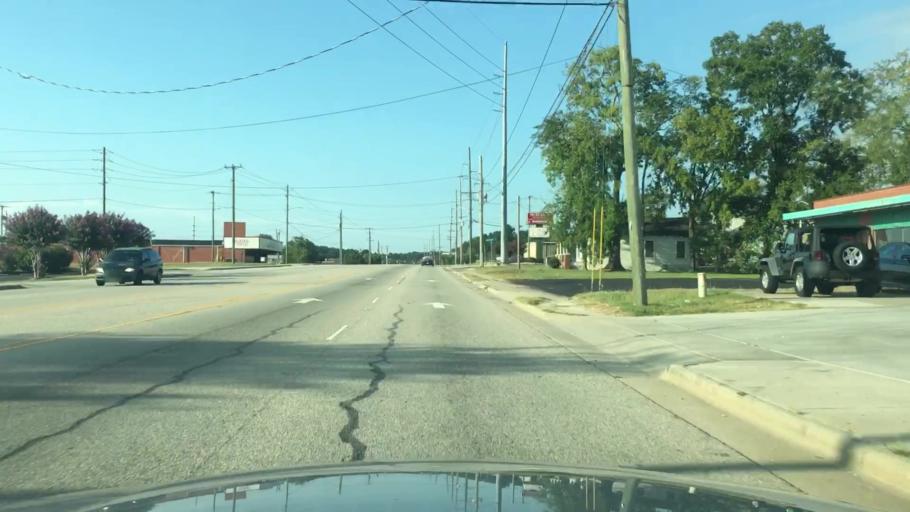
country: US
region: North Carolina
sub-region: Cumberland County
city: Fayetteville
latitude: 35.0522
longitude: -78.8885
